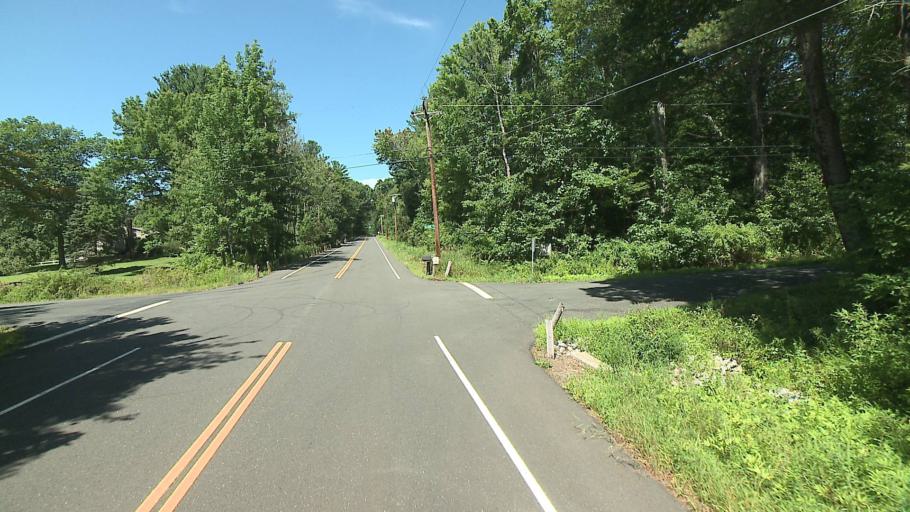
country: US
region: Connecticut
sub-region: Litchfield County
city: New Hartford Center
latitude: 41.9520
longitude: -72.9748
